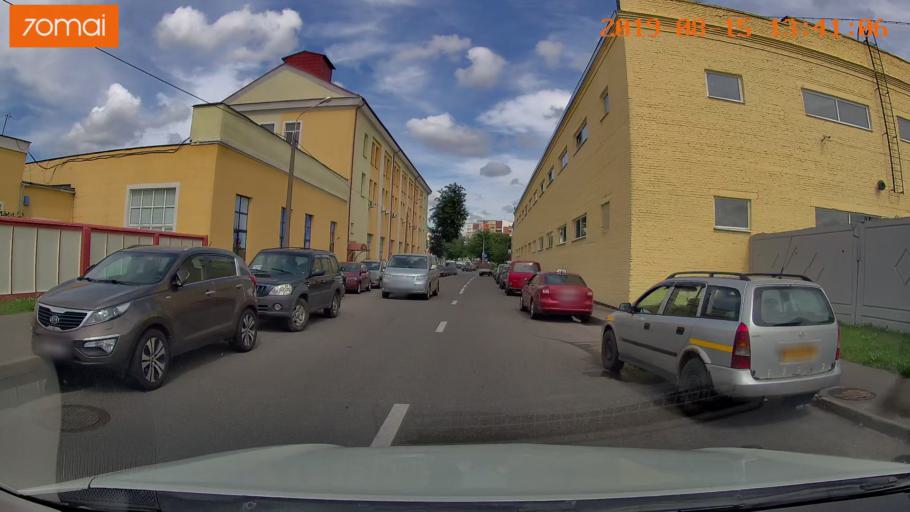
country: BY
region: Minsk
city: Minsk
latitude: 53.8839
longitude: 27.5866
